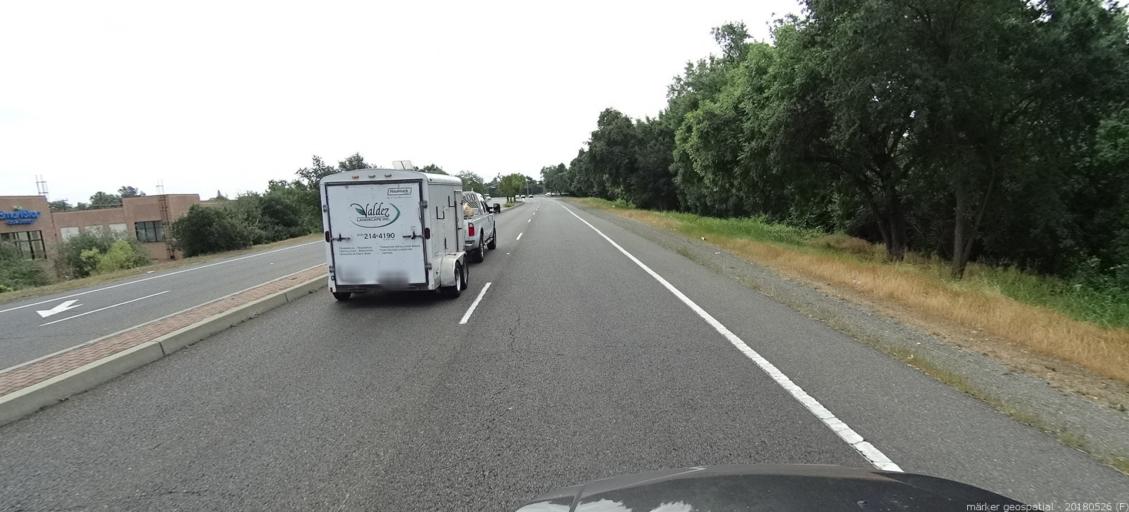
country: US
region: California
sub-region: Sacramento County
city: Sacramento
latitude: 38.6062
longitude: -121.4787
